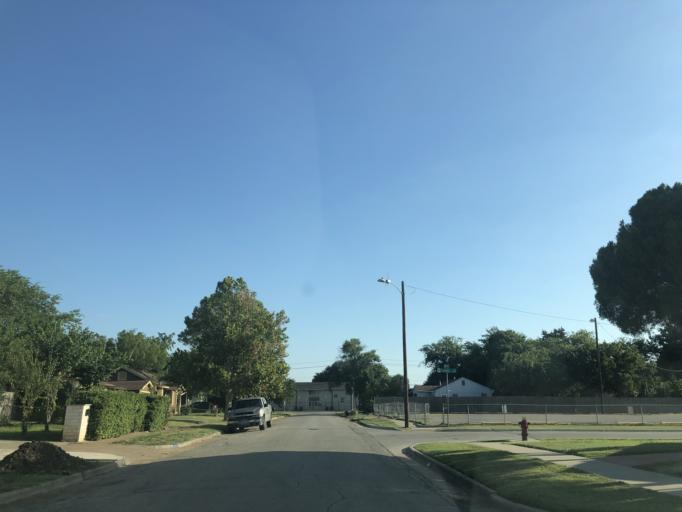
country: US
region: Texas
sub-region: Dallas County
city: Grand Prairie
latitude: 32.7338
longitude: -97.0363
